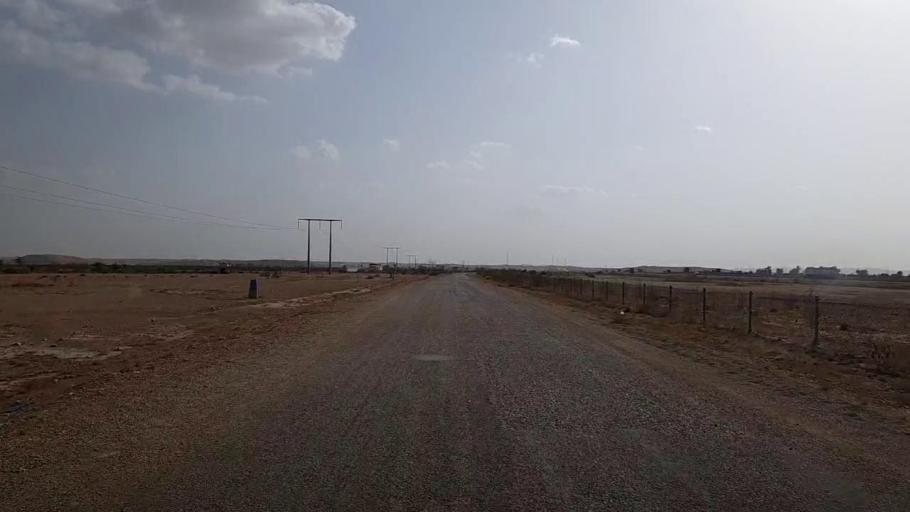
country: PK
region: Sindh
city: Kotri
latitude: 25.2654
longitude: 67.9941
